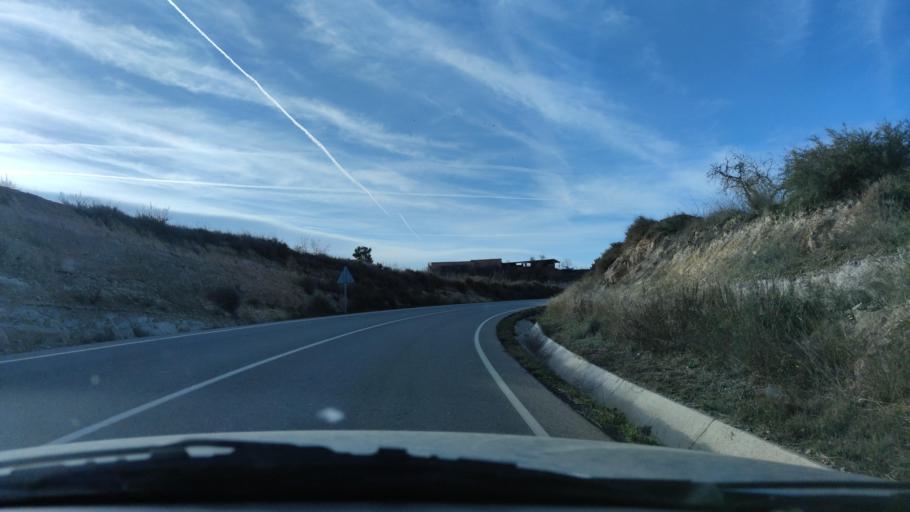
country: ES
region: Catalonia
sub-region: Provincia de Lleida
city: Aspa
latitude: 41.4941
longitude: 0.6768
